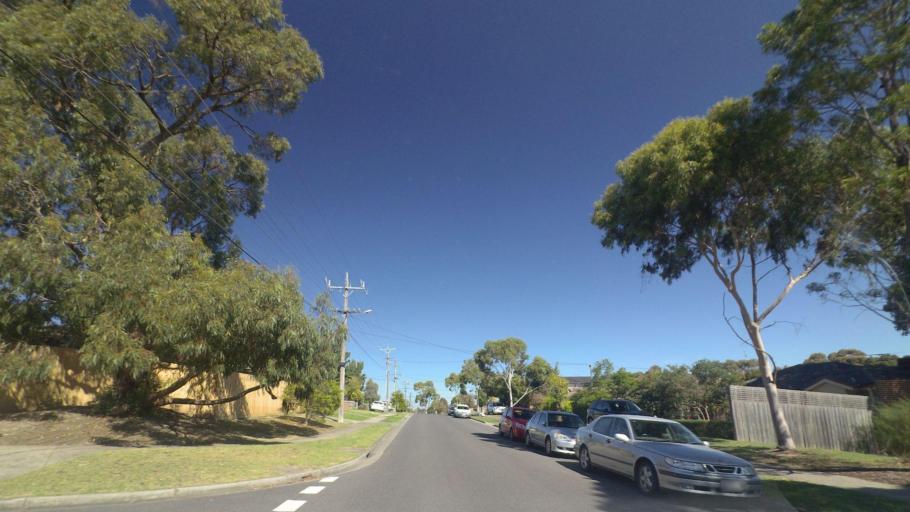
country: AU
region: Victoria
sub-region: Manningham
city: Donvale
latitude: -37.7954
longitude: 145.1700
